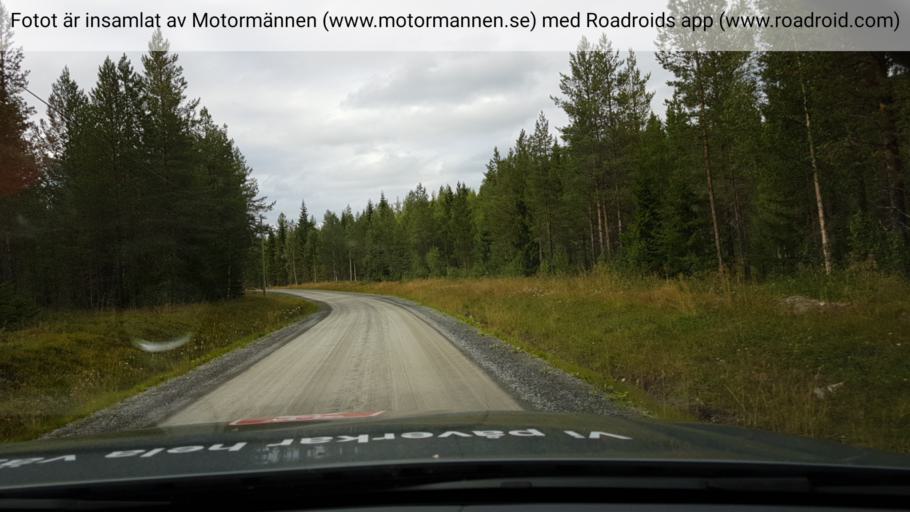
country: SE
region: Jaemtland
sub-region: Krokoms Kommun
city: Valla
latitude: 63.7079
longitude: 13.5588
